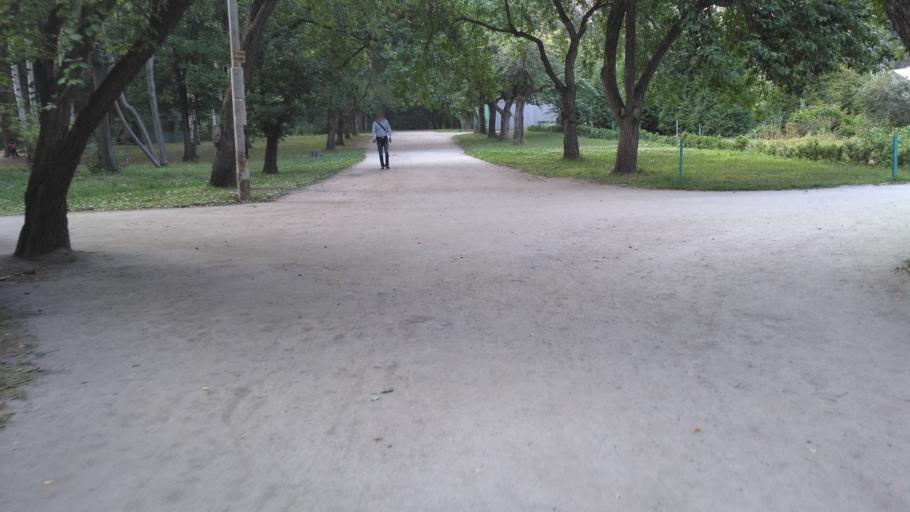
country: RU
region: Sverdlovsk
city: Yekaterinburg
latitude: 56.8477
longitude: 60.6522
